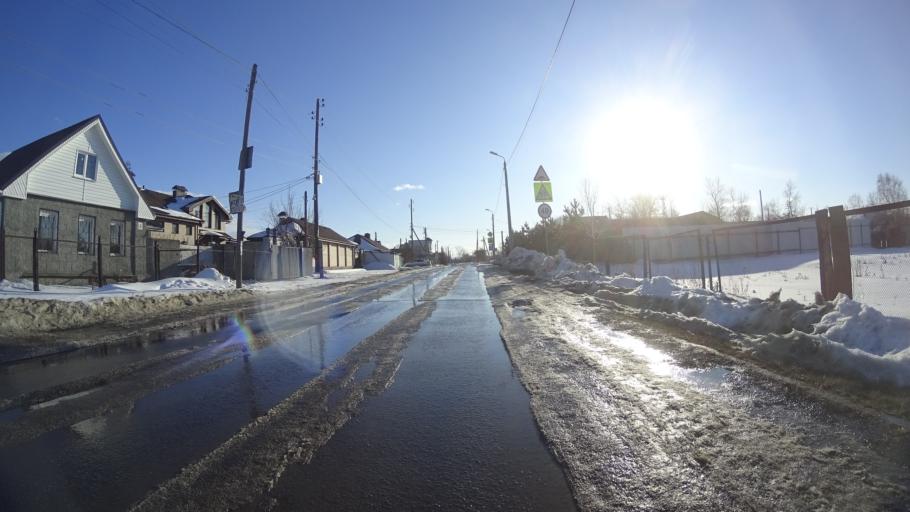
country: RU
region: Chelyabinsk
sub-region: Gorod Chelyabinsk
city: Chelyabinsk
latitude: 55.1518
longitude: 61.3091
